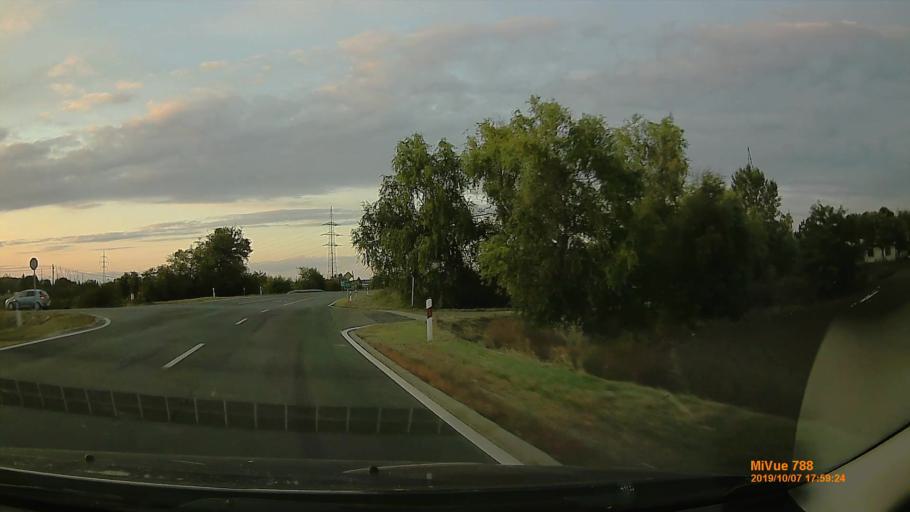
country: HU
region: Bacs-Kiskun
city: Kecskemet
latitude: 46.8777
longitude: 19.6803
